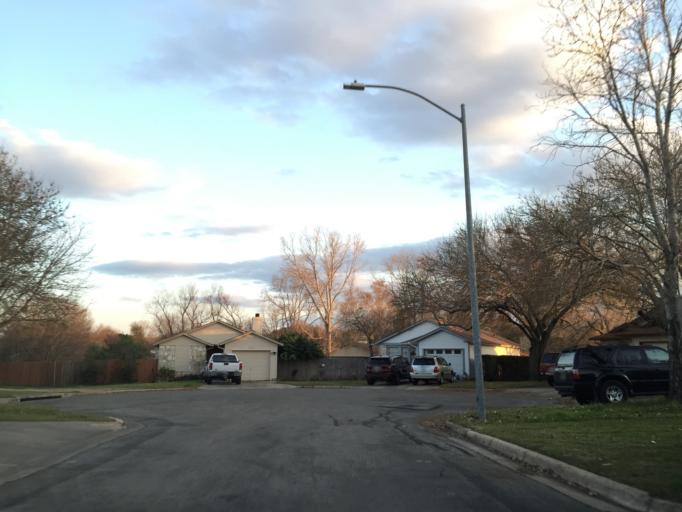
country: US
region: Texas
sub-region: Williamson County
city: Jollyville
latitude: 30.4398
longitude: -97.7404
